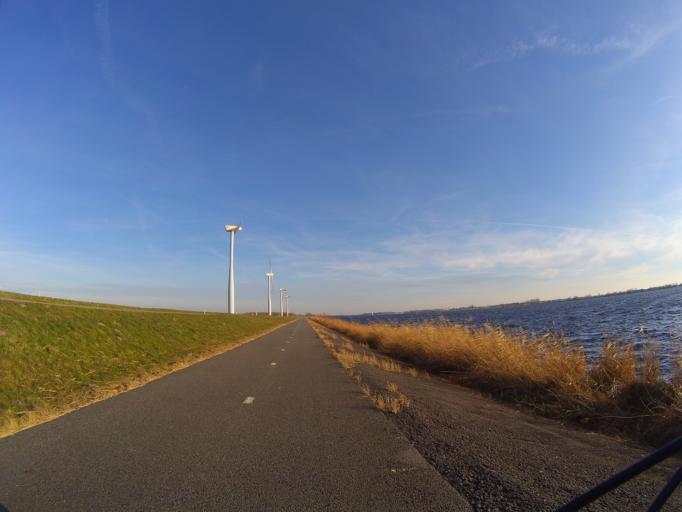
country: NL
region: Utrecht
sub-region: Gemeente Bunschoten
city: Spakenburg
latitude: 52.2756
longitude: 5.3659
